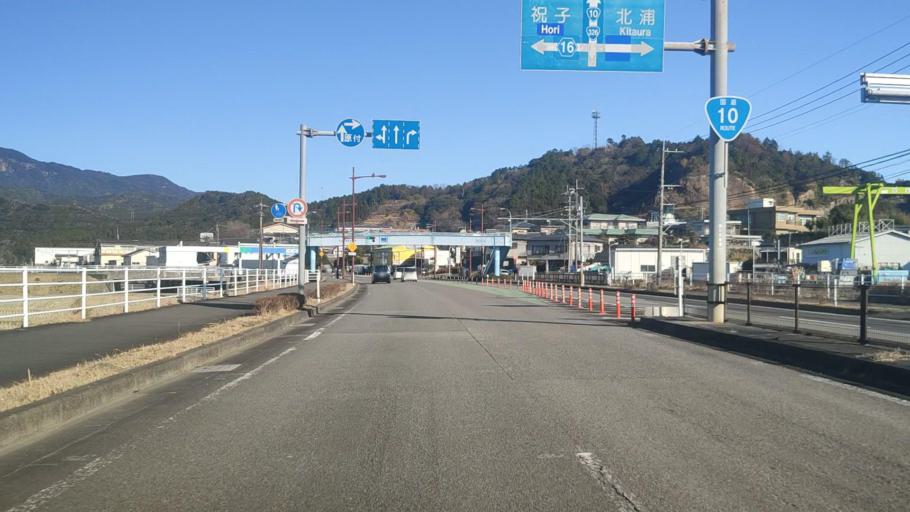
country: JP
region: Miyazaki
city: Nobeoka
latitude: 32.6087
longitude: 131.6833
